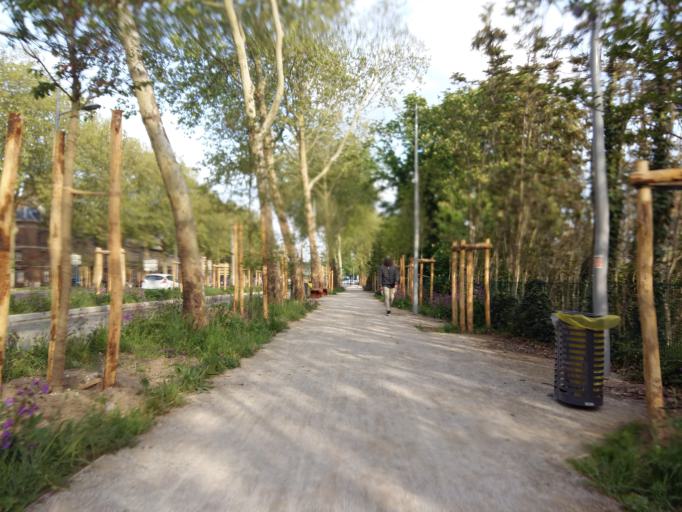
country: FR
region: Picardie
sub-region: Departement de la Somme
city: Amiens
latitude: 49.8896
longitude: 2.2926
